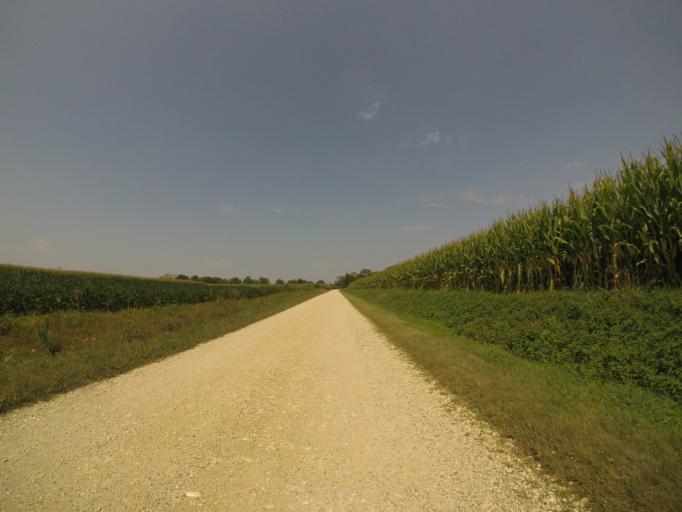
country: IT
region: Friuli Venezia Giulia
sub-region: Provincia di Udine
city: Talmassons
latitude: 45.9381
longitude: 13.1076
